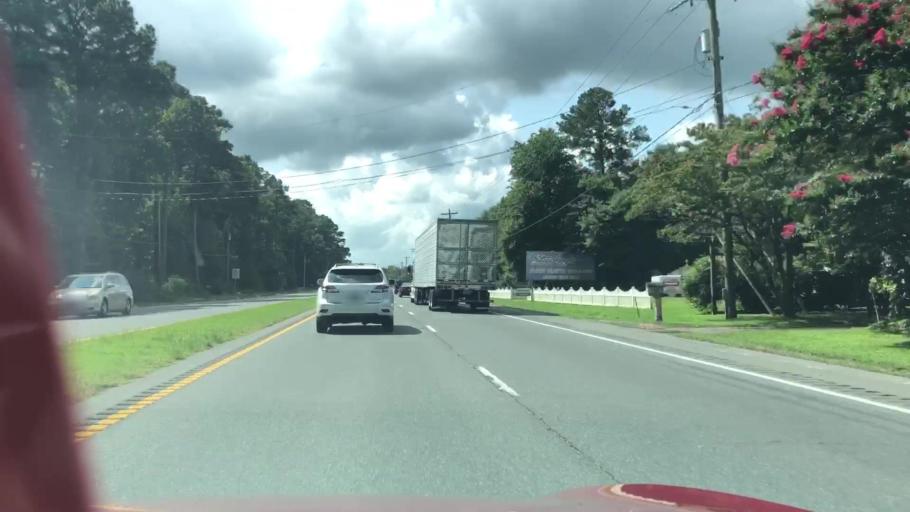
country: US
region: Virginia
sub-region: Accomack County
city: Wattsville
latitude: 37.8999
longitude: -75.5490
